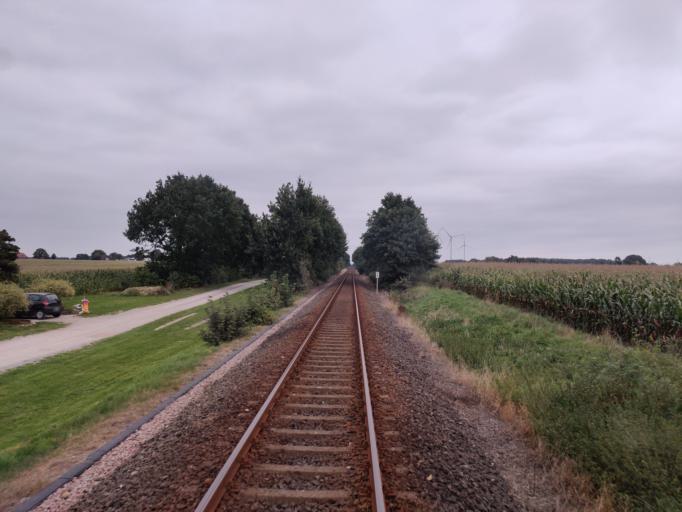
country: DE
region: Lower Saxony
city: Kutenholz
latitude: 53.4965
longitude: 9.2982
